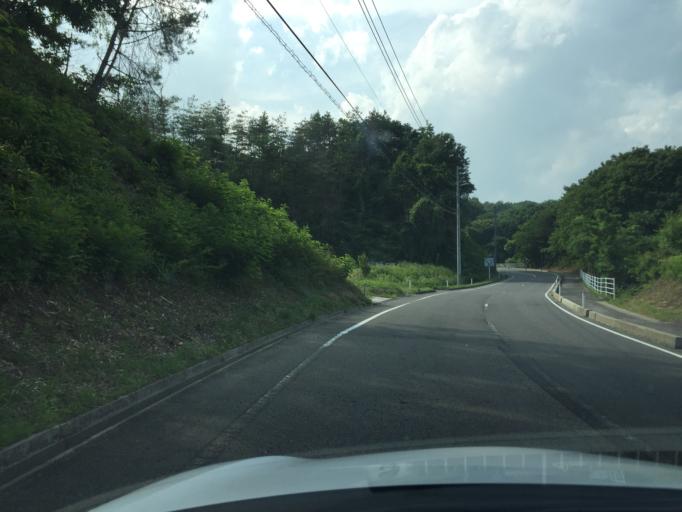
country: JP
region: Fukushima
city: Miharu
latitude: 37.3961
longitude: 140.4820
